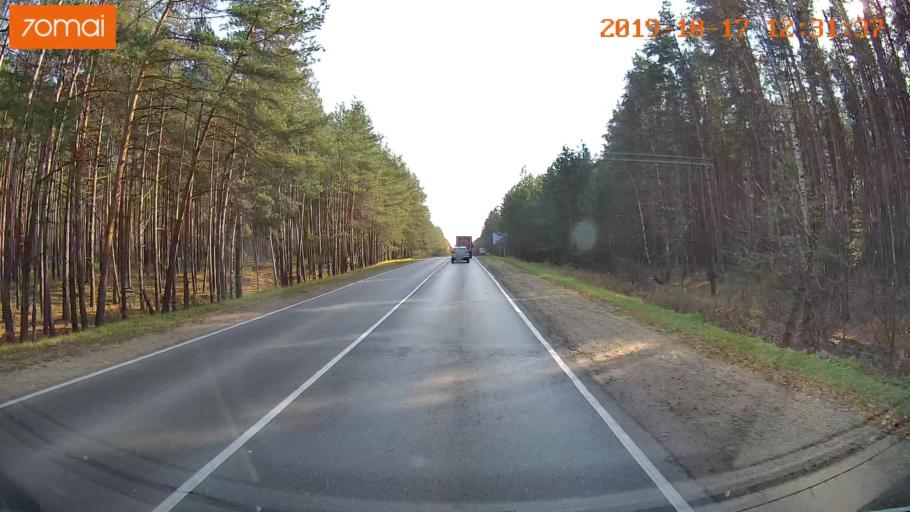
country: RU
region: Rjazan
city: Syntul
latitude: 54.9668
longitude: 41.3358
